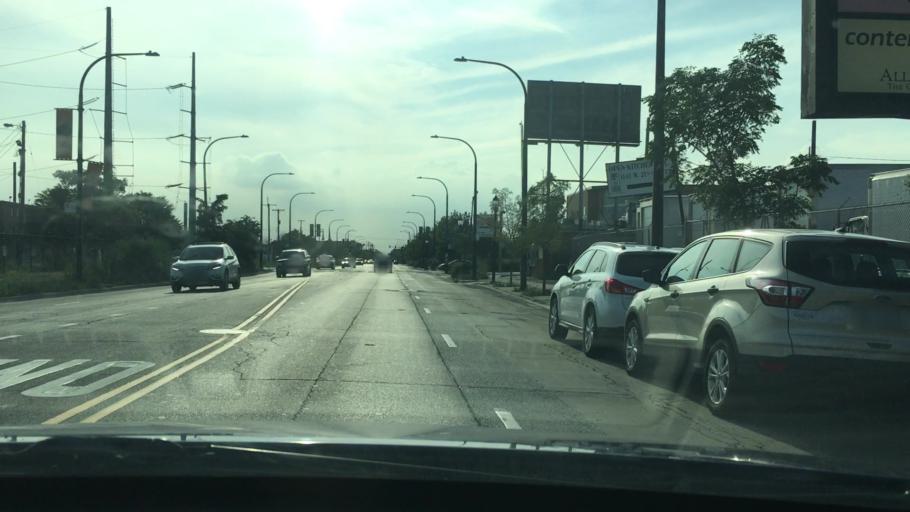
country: US
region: Illinois
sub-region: Cook County
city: Chicago
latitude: 41.8526
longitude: -87.6551
